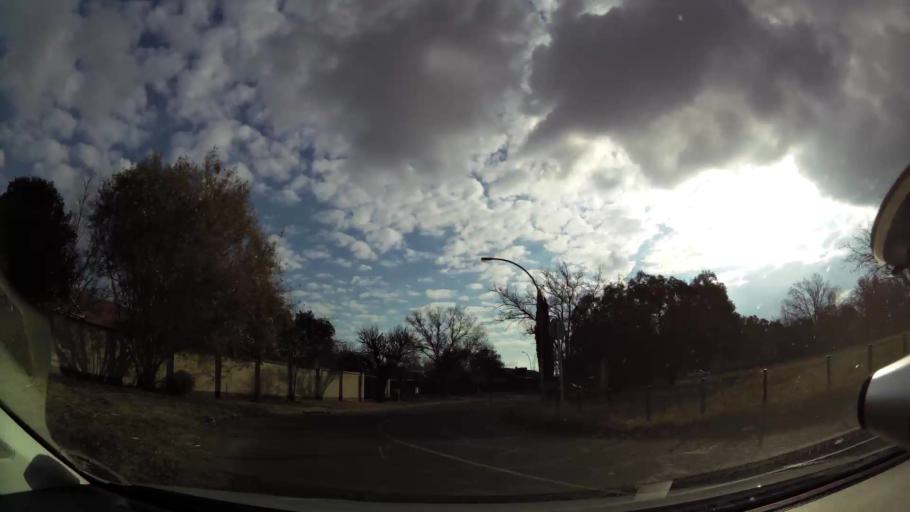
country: ZA
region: Orange Free State
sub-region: Mangaung Metropolitan Municipality
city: Bloemfontein
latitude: -29.1013
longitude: 26.2021
